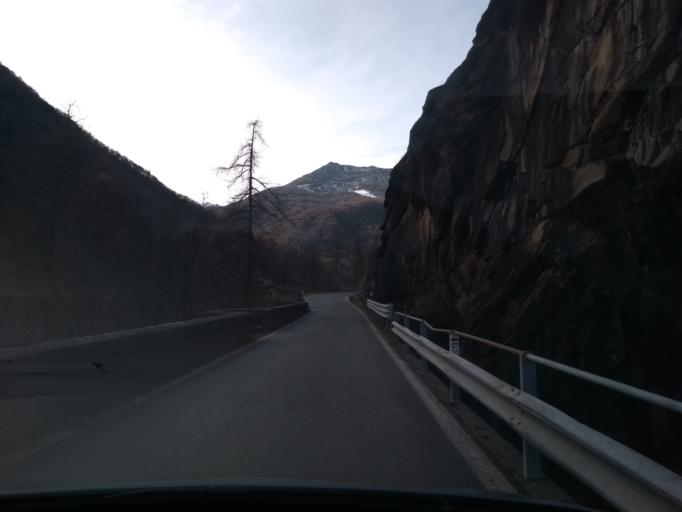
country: IT
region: Piedmont
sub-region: Provincia di Torino
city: Ala di Stura
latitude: 45.3159
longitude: 7.3314
